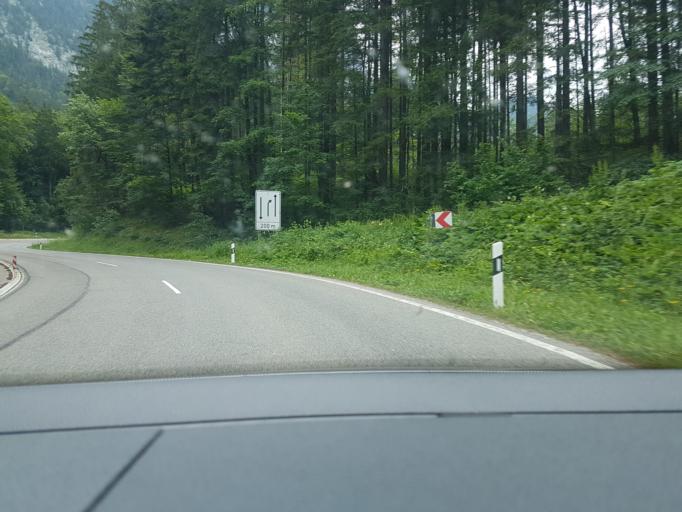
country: DE
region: Bavaria
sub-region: Upper Bavaria
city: Bayerisch Gmain
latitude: 47.7055
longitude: 12.9298
